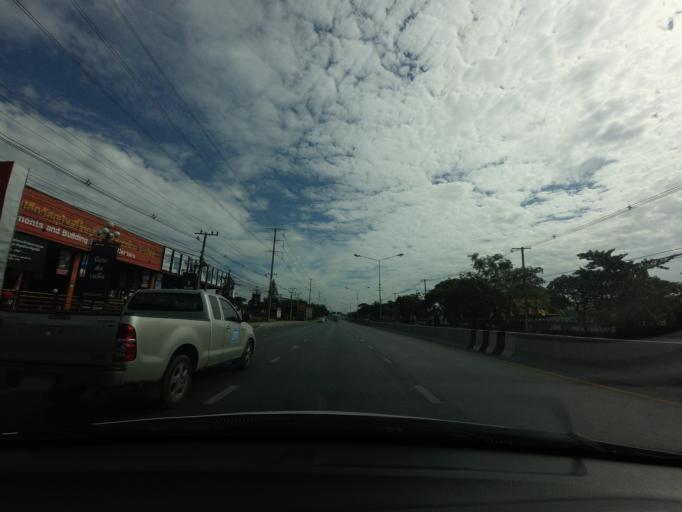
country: TH
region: Pathum Thani
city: Ban Rangsit
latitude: 14.0268
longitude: 100.7498
